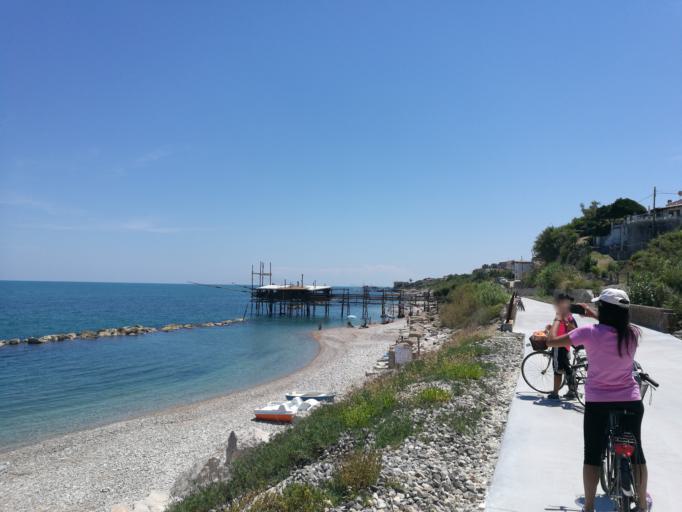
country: IT
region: Abruzzo
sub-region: Provincia di Chieti
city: Marina di San Vito
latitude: 42.2917
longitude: 14.4730
